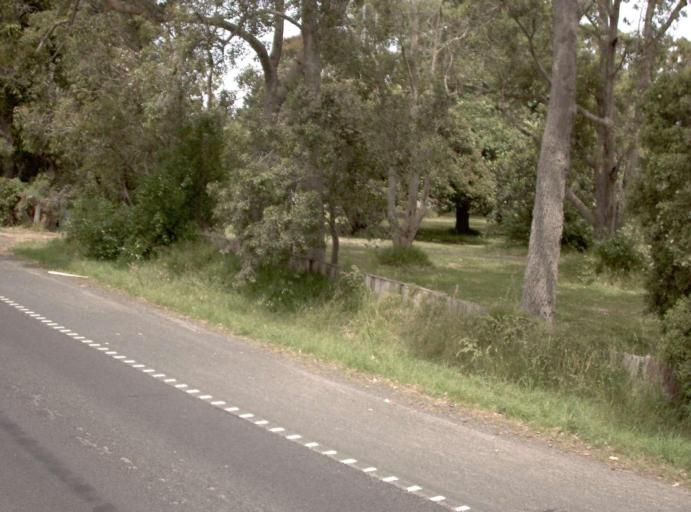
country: AU
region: Victoria
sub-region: Mornington Peninsula
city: Tyabb
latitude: -38.2364
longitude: 145.2153
